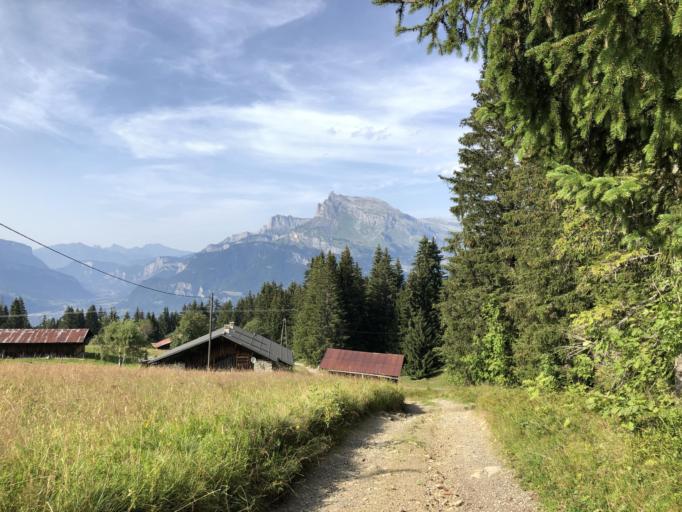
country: FR
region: Rhone-Alpes
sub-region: Departement de la Haute-Savoie
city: Combloux
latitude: 45.8751
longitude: 6.6608
